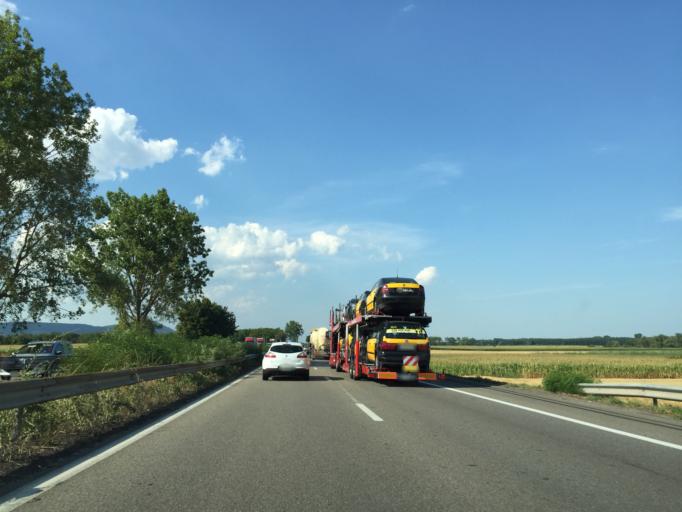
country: FR
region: Alsace
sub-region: Departement du Haut-Rhin
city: Guemar
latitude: 48.1976
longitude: 7.3972
